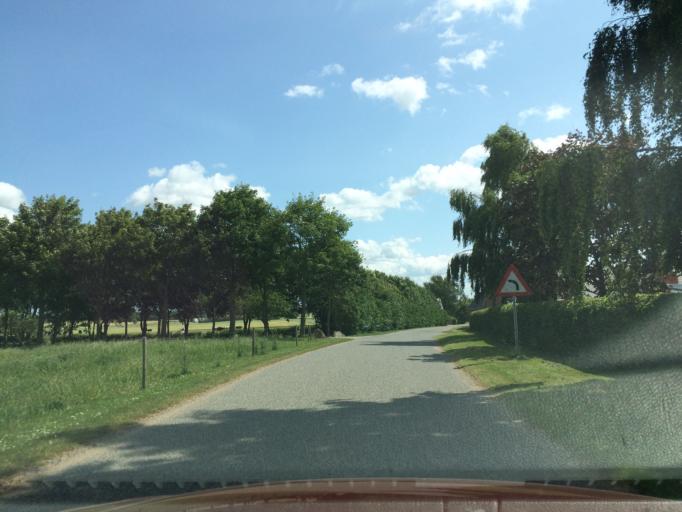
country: DK
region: Central Jutland
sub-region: Viborg Kommune
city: Bjerringbro
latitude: 56.2608
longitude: 9.6954
